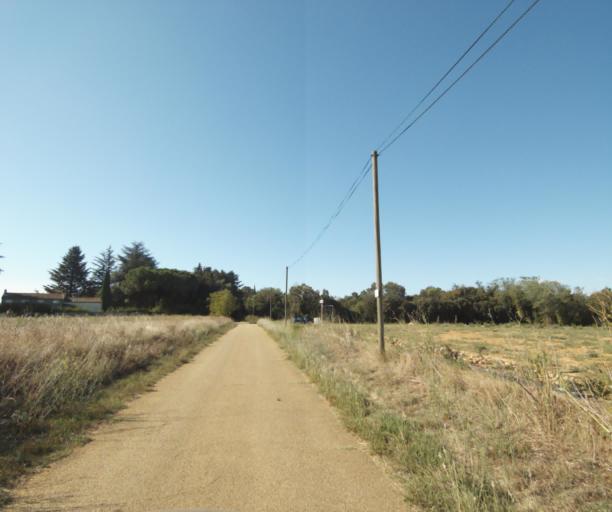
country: FR
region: Languedoc-Roussillon
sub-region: Departement du Gard
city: Bouillargues
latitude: 43.7922
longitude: 4.4178
